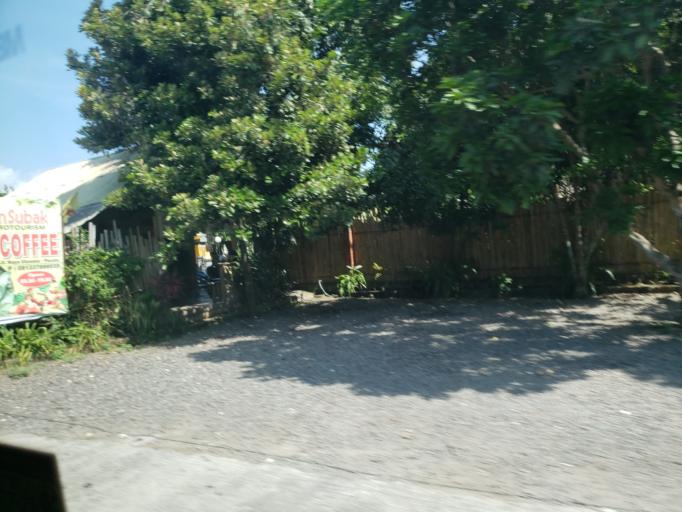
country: ID
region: Bali
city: Kangin
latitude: -8.8291
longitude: 115.1373
